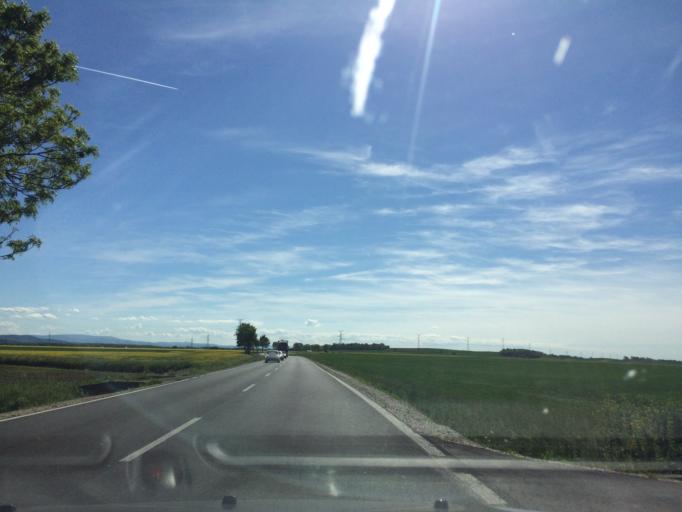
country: PL
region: Lower Silesian Voivodeship
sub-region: Powiat wroclawski
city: Sobotka
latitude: 50.9425
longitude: 16.7221
